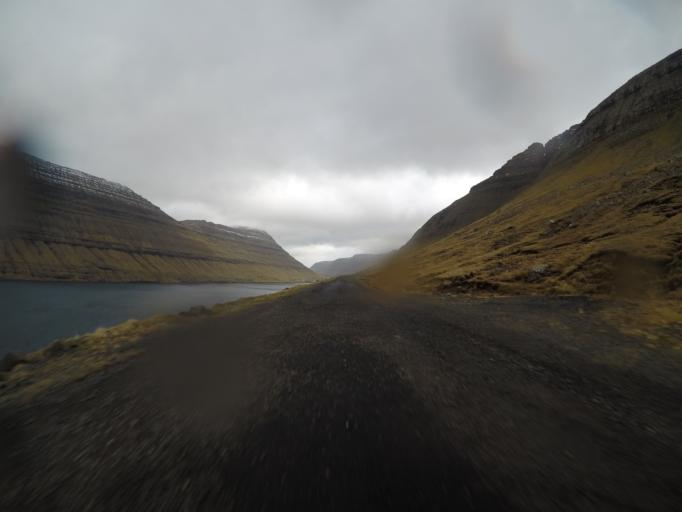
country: FO
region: Nordoyar
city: Klaksvik
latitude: 62.3158
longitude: -6.5538
